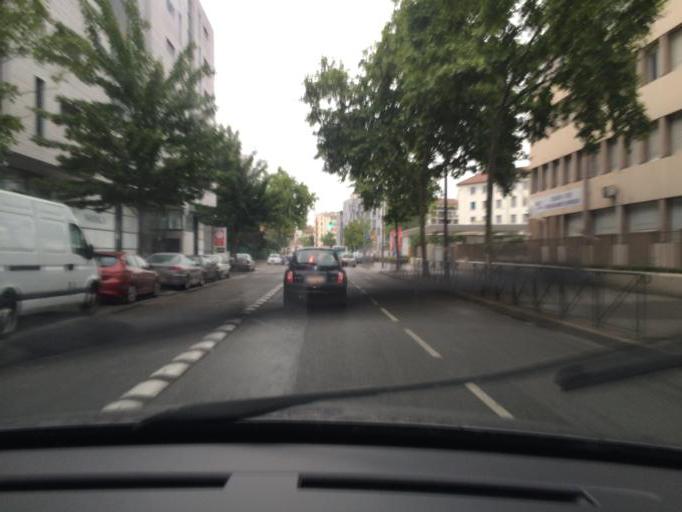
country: FR
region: Rhone-Alpes
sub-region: Departement du Rhone
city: Lyon
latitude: 45.7377
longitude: 4.8681
